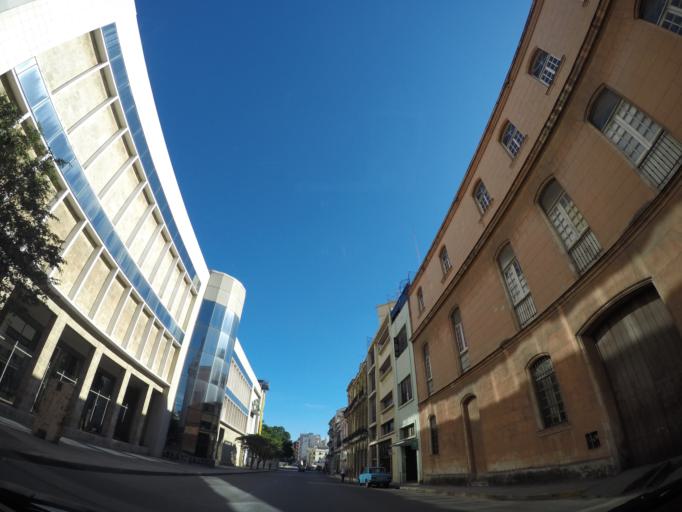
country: CU
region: La Habana
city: Centro Habana
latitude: 23.1397
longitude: -82.3571
